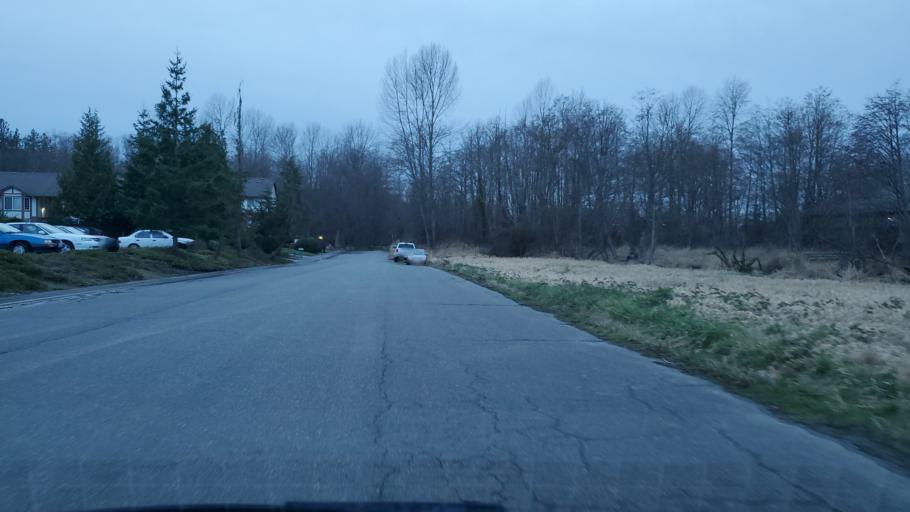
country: US
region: Washington
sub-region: Skagit County
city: Mount Vernon
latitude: 48.4327
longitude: -122.3224
